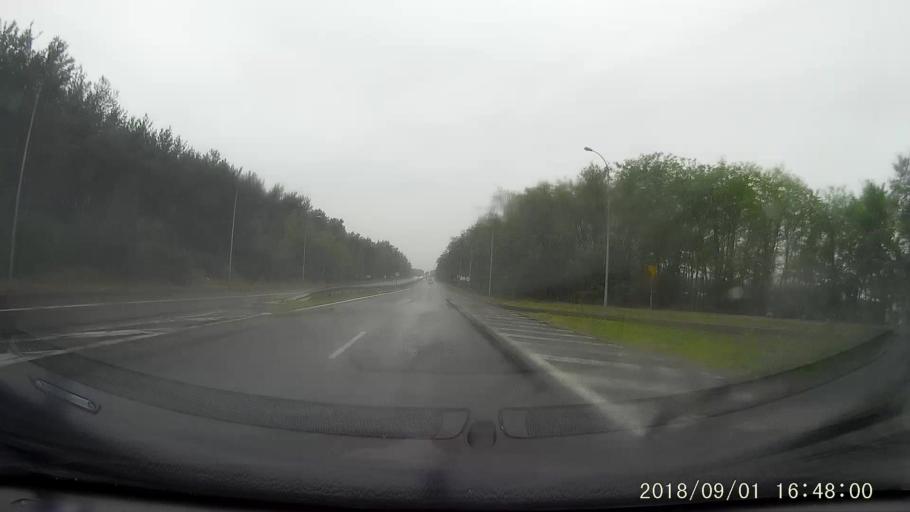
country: PL
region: Lubusz
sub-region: Zielona Gora
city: Zielona Gora
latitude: 51.9571
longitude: 15.5389
